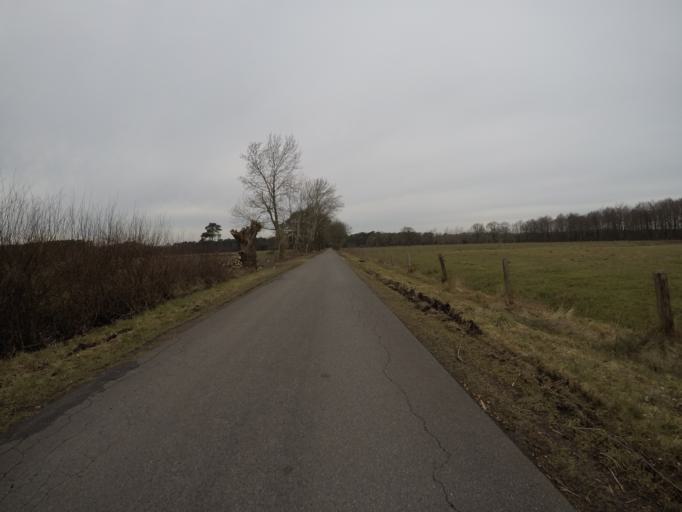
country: DE
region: North Rhine-Westphalia
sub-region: Regierungsbezirk Munster
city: Rhede
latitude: 51.7776
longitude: 6.6620
